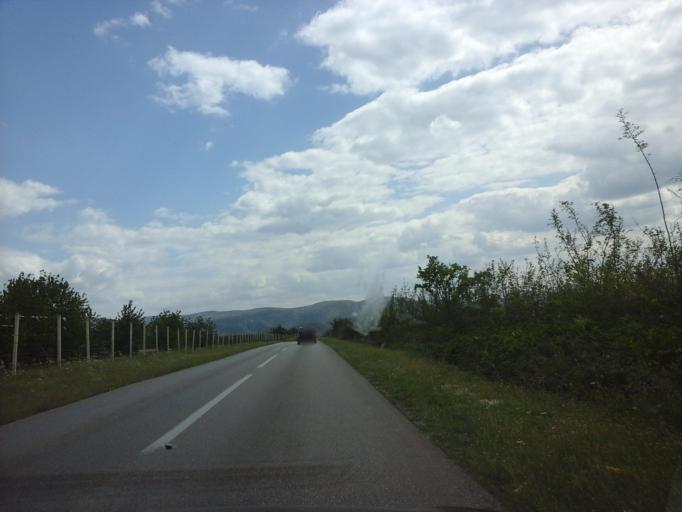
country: BA
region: Federation of Bosnia and Herzegovina
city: Blagaj
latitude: 43.2803
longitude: 17.8532
